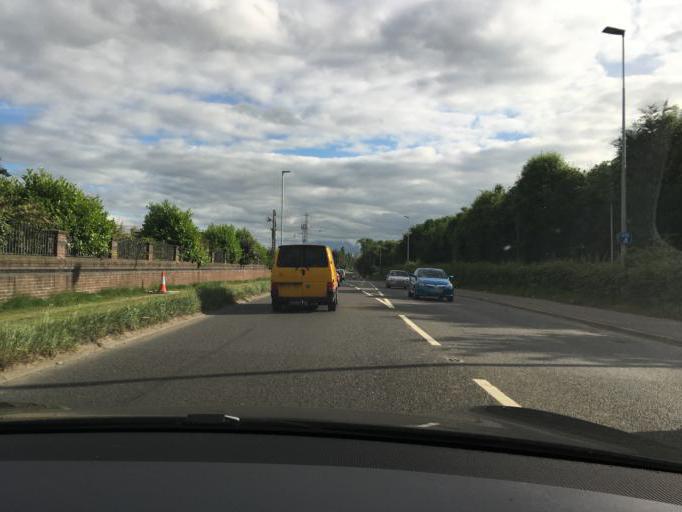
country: GB
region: England
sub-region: City and Borough of Salford
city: Irlam
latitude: 53.4614
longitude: -2.3988
